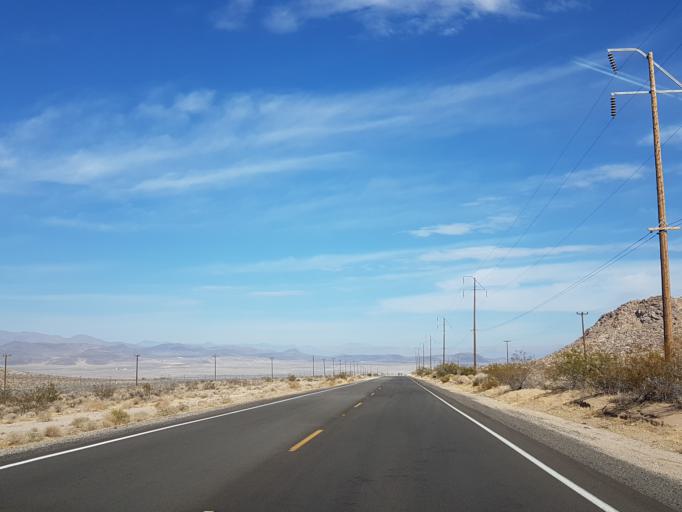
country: US
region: California
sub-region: Kern County
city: Ridgecrest
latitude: 35.6324
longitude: -117.5791
